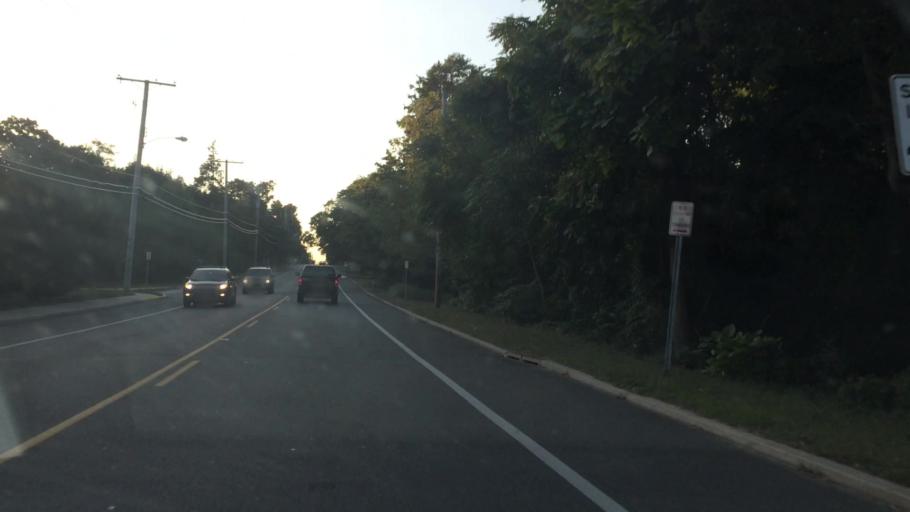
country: US
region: New Jersey
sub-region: Ocean County
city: Barnegat
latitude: 39.7544
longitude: -74.2279
